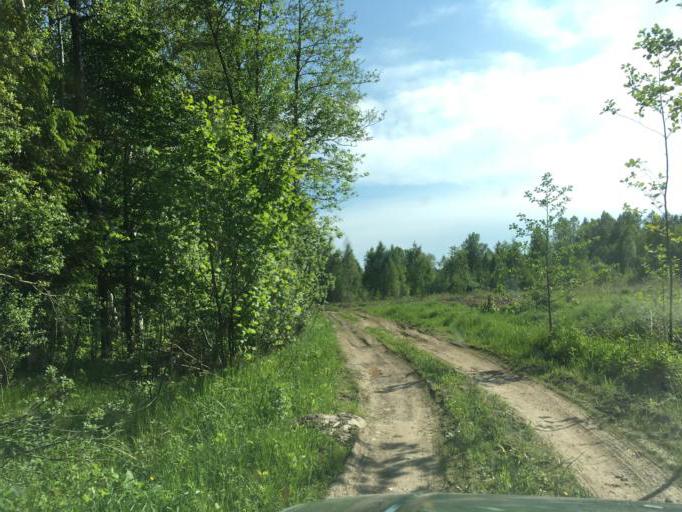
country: LV
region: Dundaga
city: Dundaga
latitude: 57.6026
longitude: 22.5080
